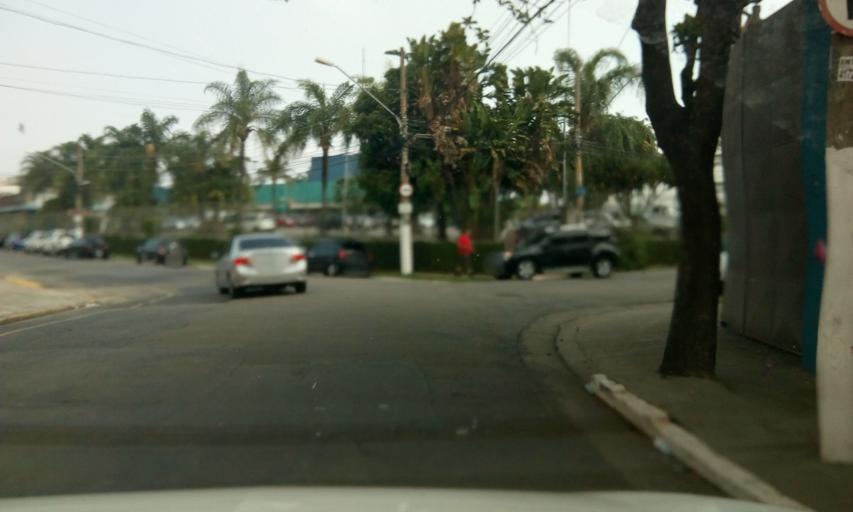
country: BR
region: Sao Paulo
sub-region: Osasco
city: Osasco
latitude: -23.5375
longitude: -46.7290
